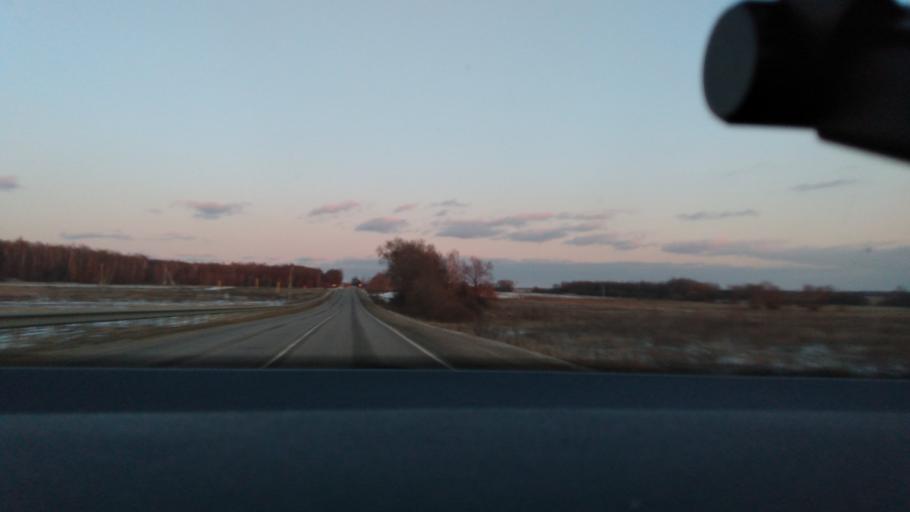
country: RU
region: Moskovskaya
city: Lukhovitsy
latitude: 55.0950
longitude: 38.9608
